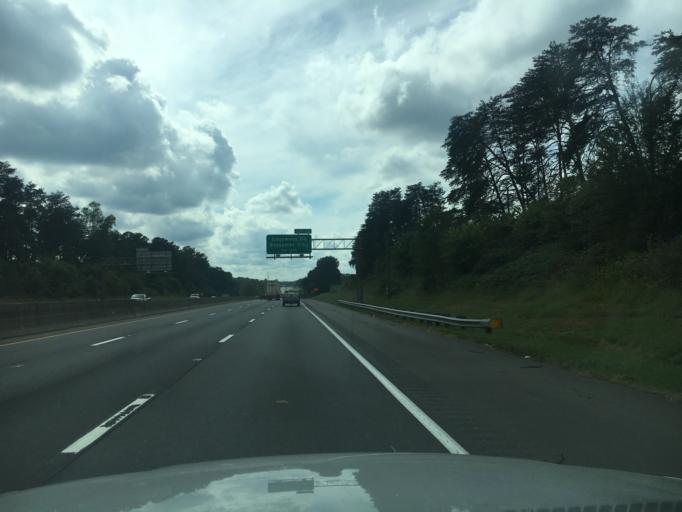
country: US
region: North Carolina
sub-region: Gaston County
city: Bessemer City
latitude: 35.2729
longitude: -81.2407
